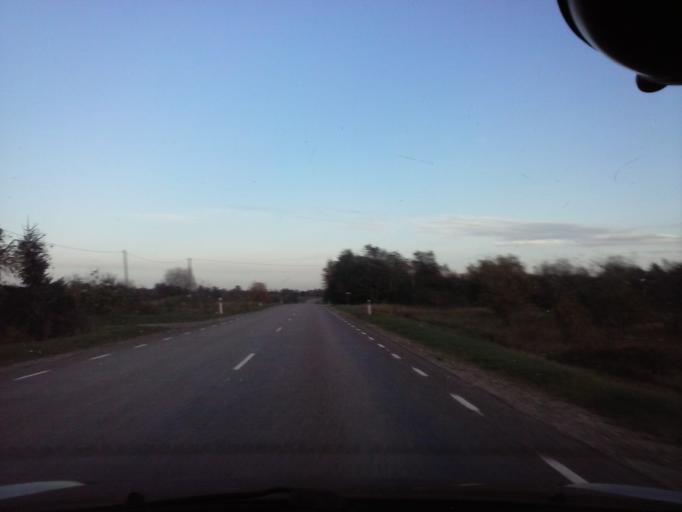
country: EE
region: Harju
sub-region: Nissi vald
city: Turba
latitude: 58.9171
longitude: 24.1780
